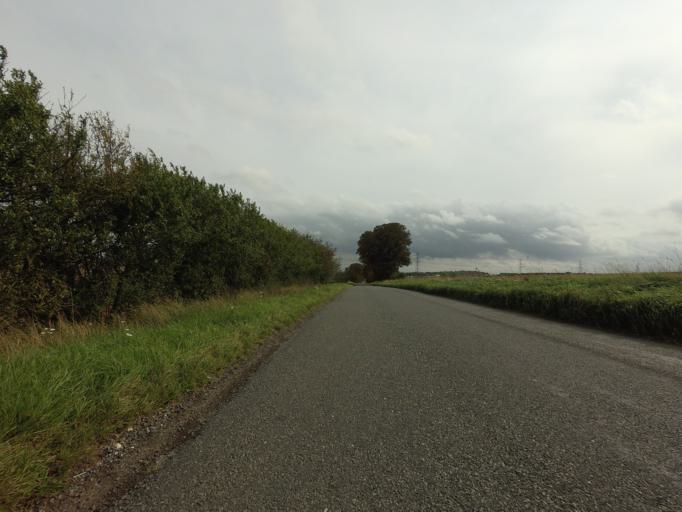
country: GB
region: England
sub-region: Essex
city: Saffron Walden
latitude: 52.0242
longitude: 0.1885
